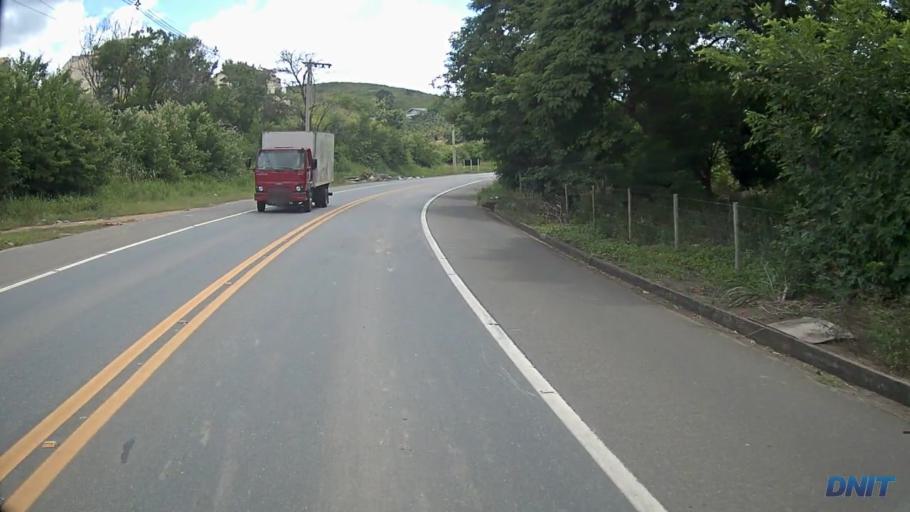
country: BR
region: Minas Gerais
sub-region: Governador Valadares
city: Governador Valadares
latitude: -18.8461
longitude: -41.9763
